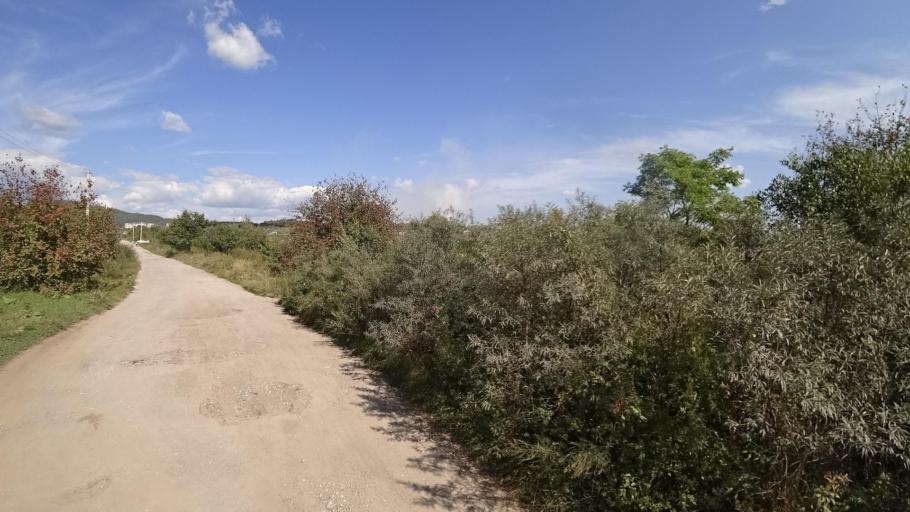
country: RU
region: Jewish Autonomous Oblast
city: Londoko
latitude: 49.0042
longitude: 131.8698
